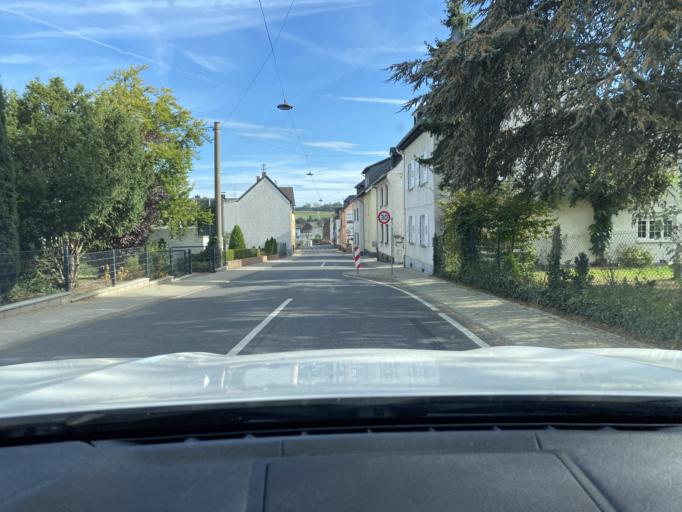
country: DE
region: Rheinland-Pfalz
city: Plaidt
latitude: 50.4040
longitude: 7.4077
